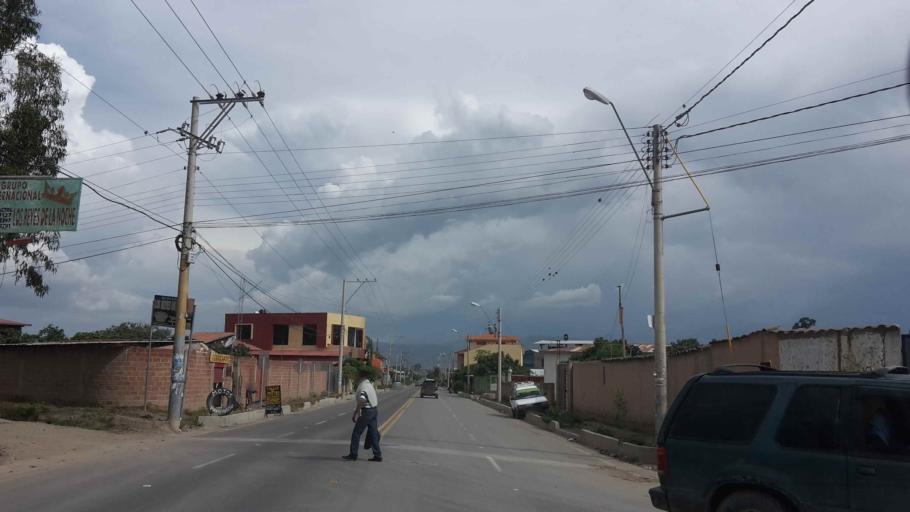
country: BO
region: Cochabamba
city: Cochabamba
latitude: -17.3395
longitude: -66.2626
